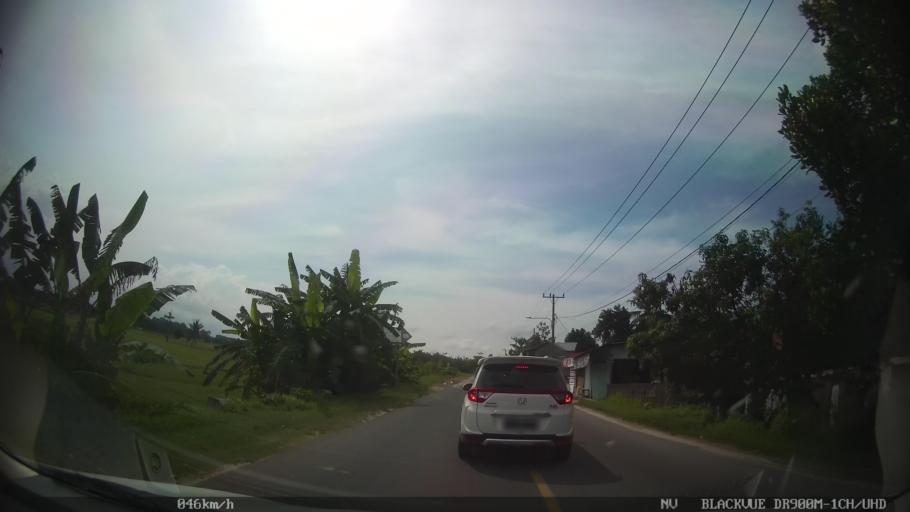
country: ID
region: North Sumatra
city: Percut
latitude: 3.6116
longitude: 98.8462
